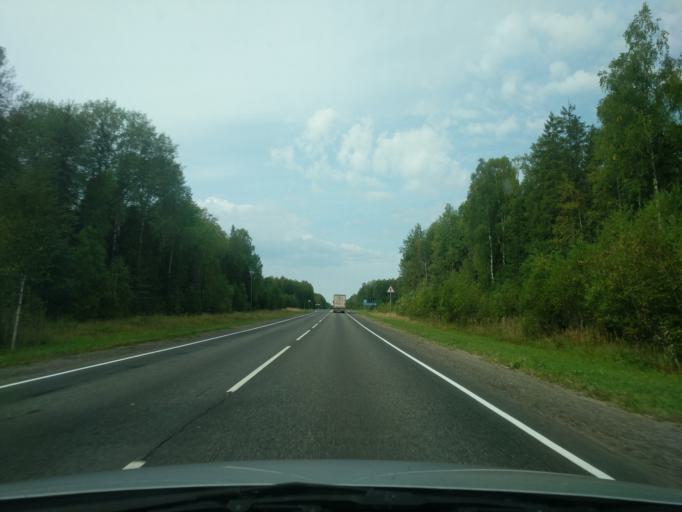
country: RU
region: Kirov
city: Leninskoye
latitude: 58.3188
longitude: 46.8815
